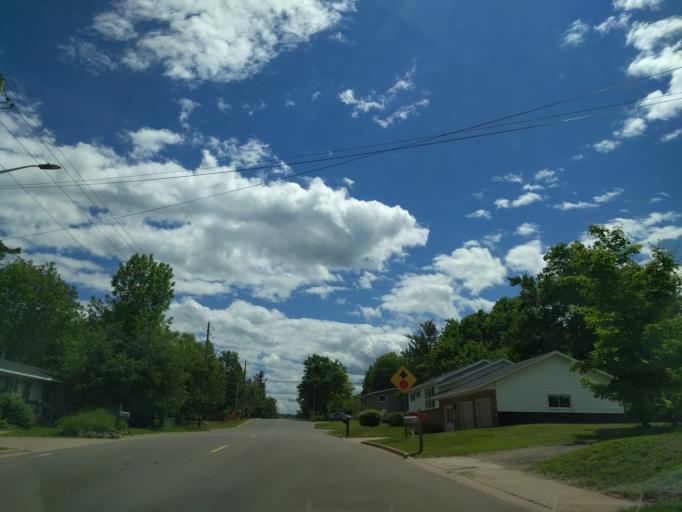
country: US
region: Michigan
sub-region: Marquette County
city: Trowbridge Park
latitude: 46.5533
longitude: -87.4198
